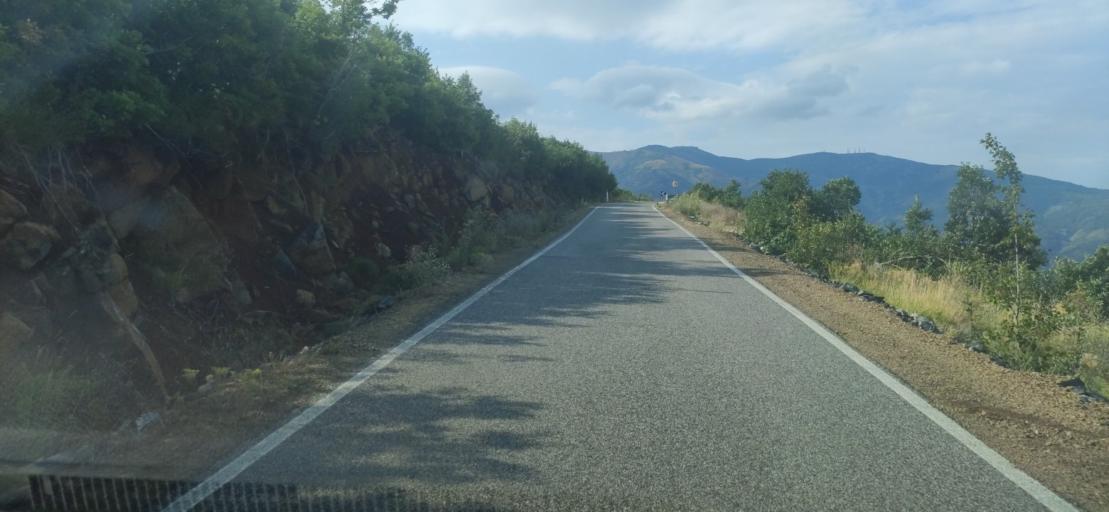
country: AL
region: Shkoder
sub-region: Rrethi i Pukes
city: Iballe
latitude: 42.1695
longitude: 20.0030
